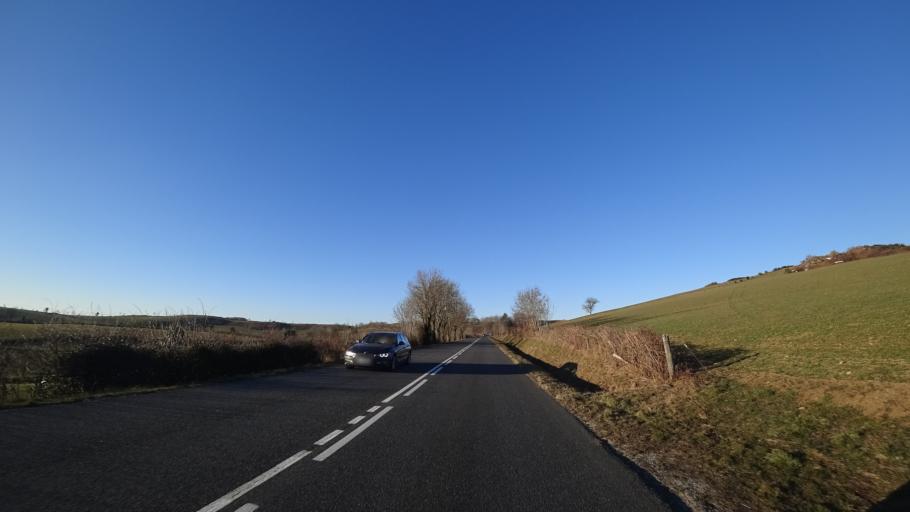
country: FR
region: Midi-Pyrenees
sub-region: Departement de l'Aveyron
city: Pont-de-Salars
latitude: 44.3335
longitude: 2.7650
